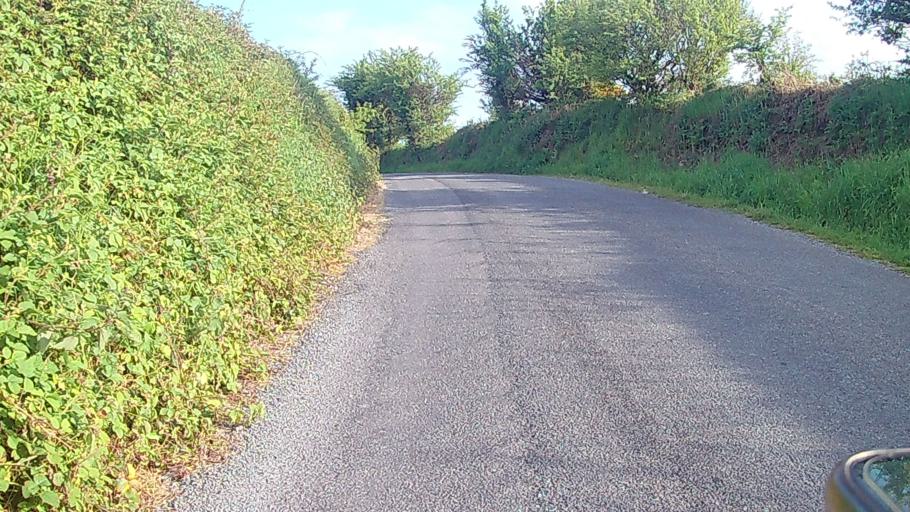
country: IE
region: Munster
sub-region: County Cork
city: Cork
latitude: 51.9754
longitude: -8.4634
